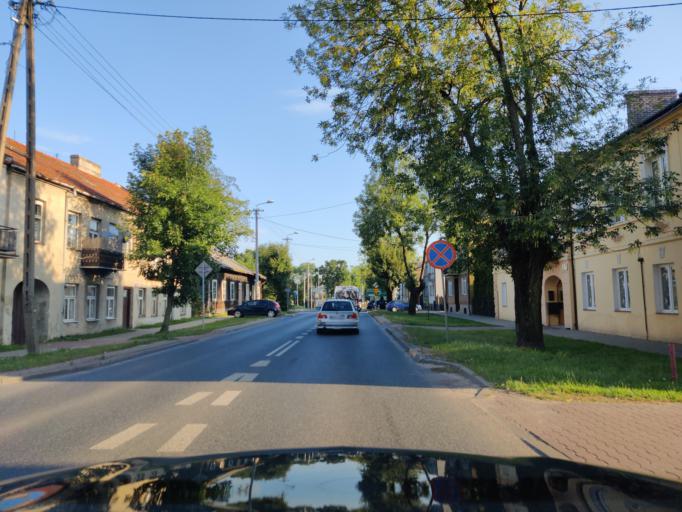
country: PL
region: Masovian Voivodeship
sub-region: Powiat pultuski
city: Pultusk
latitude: 52.7089
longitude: 21.0836
